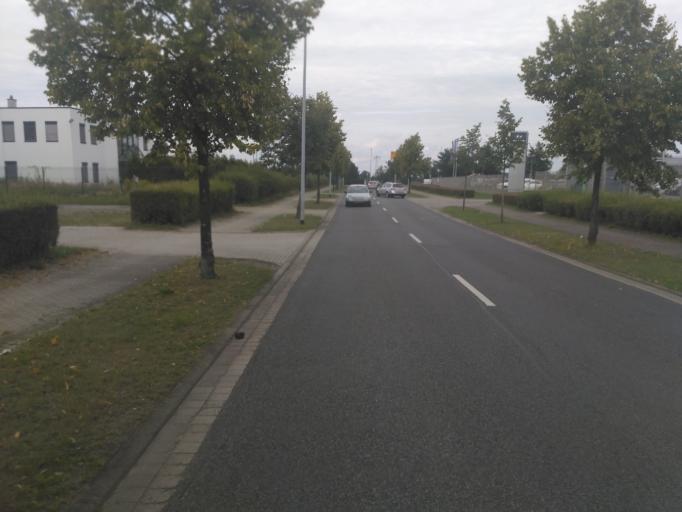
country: DE
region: Saxony
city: Hoyerswerda
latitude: 51.4505
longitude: 14.2188
